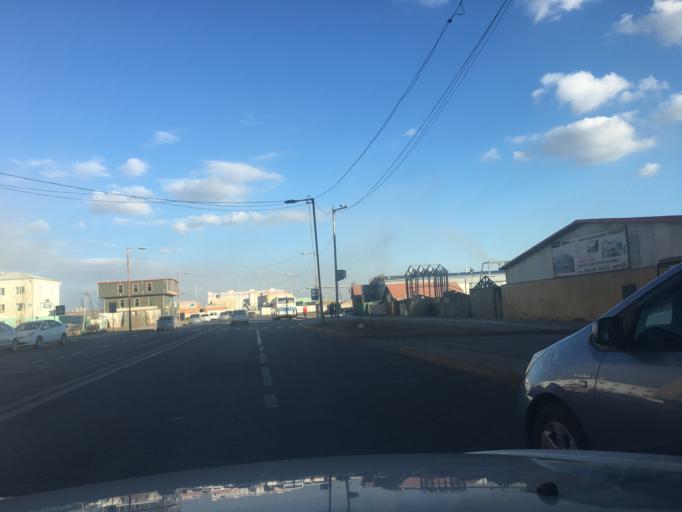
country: MN
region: Ulaanbaatar
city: Ulaanbaatar
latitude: 47.9105
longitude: 106.7863
